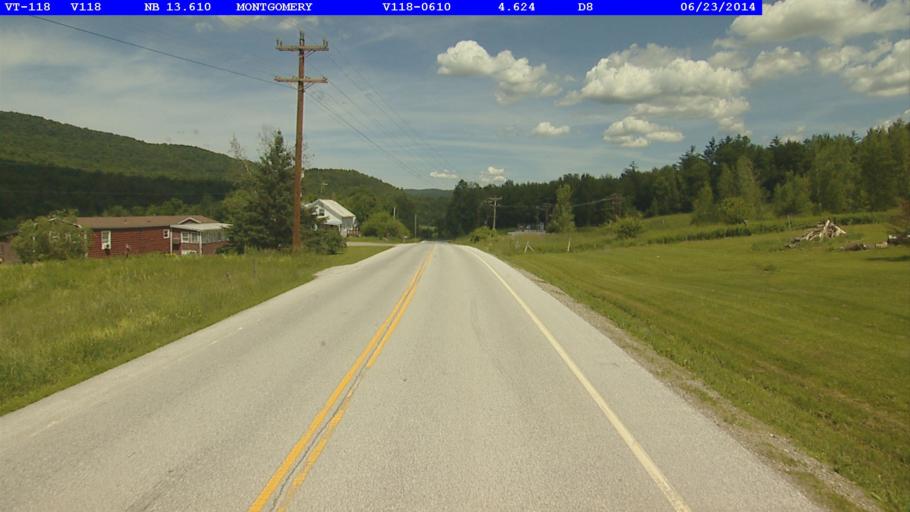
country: US
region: Vermont
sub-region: Franklin County
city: Richford
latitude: 44.8641
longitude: -72.6097
